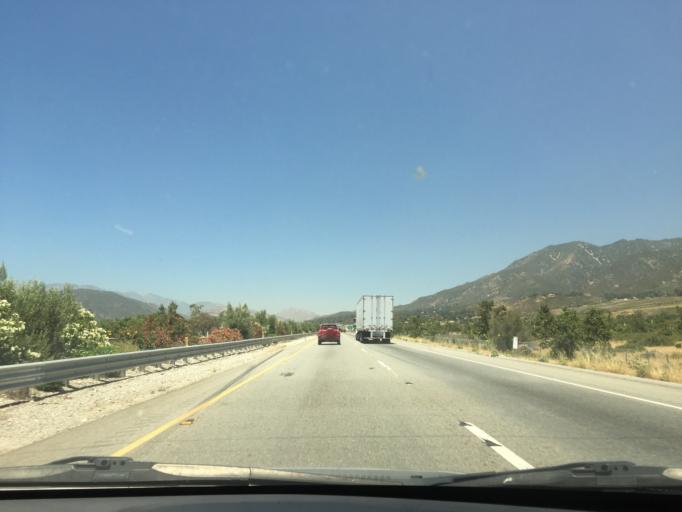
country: US
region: California
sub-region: San Bernardino County
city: Muscoy
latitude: 34.2117
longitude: -117.3880
